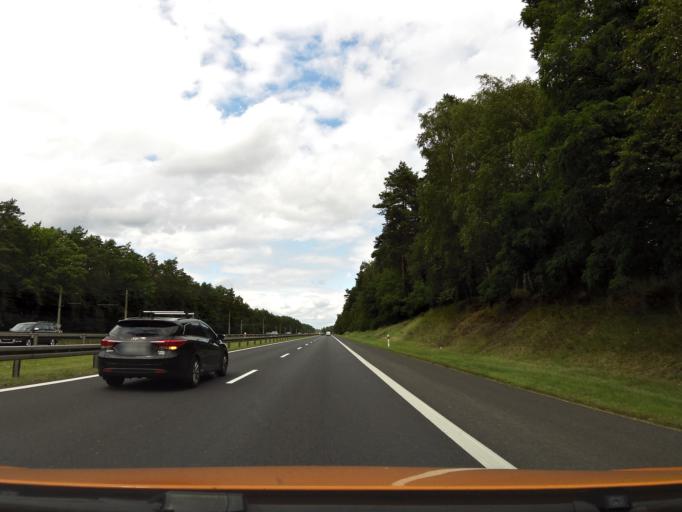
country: PL
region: West Pomeranian Voivodeship
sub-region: Powiat goleniowski
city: Goleniow
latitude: 53.5112
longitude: 14.8029
